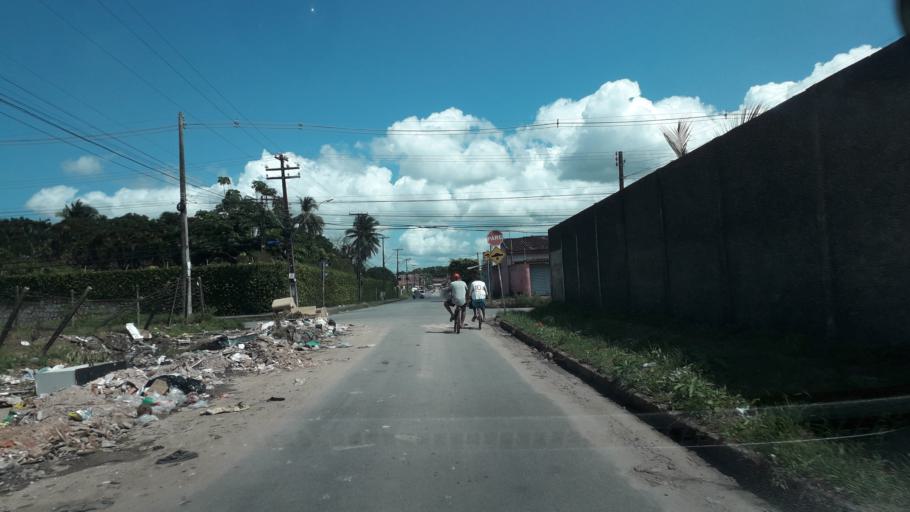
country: BR
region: Alagoas
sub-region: Satuba
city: Satuba
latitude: -9.5557
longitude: -35.7845
